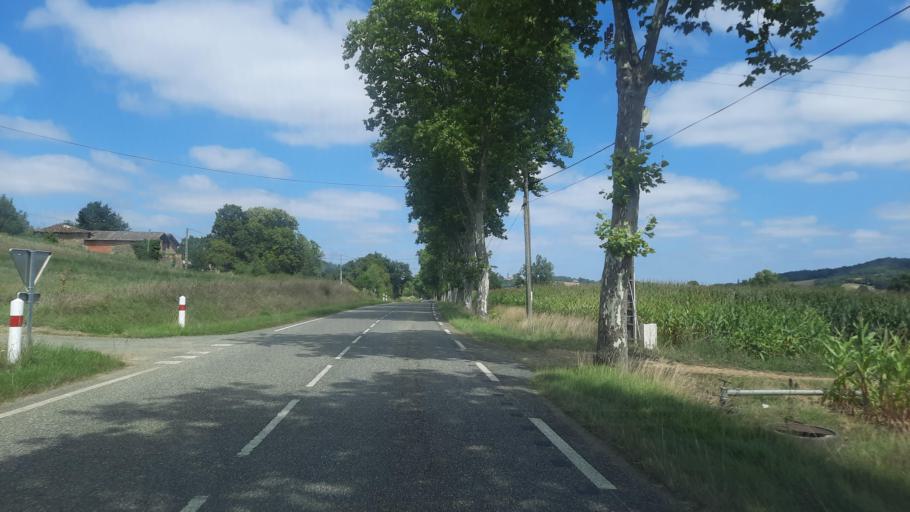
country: FR
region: Midi-Pyrenees
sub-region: Departement de la Haute-Garonne
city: Boulogne-sur-Gesse
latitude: 43.3614
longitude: 0.7352
